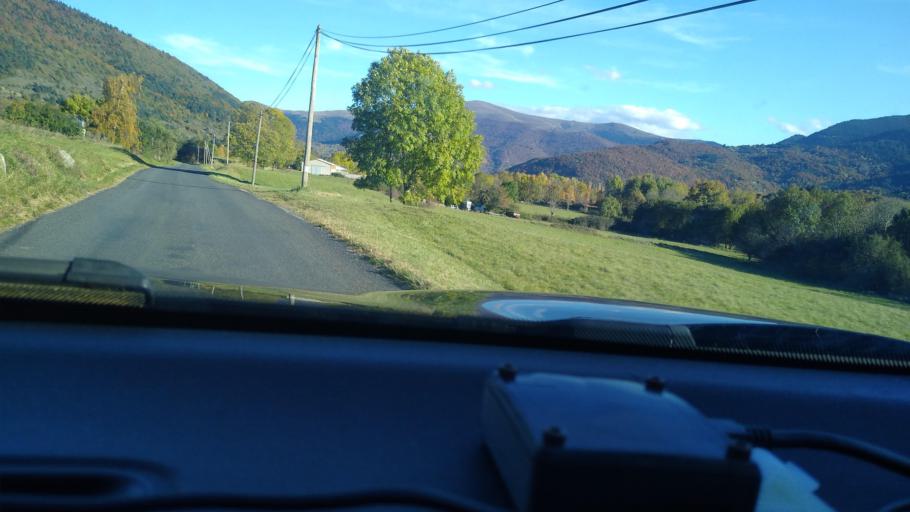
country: FR
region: Languedoc-Roussillon
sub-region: Departement de l'Aude
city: Quillan
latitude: 42.7456
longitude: 2.1844
